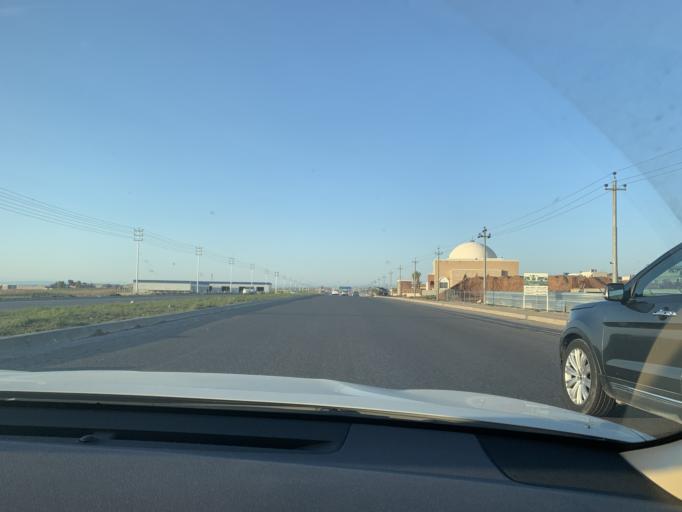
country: IQ
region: Arbil
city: Erbil
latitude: 36.2780
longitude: 44.0156
